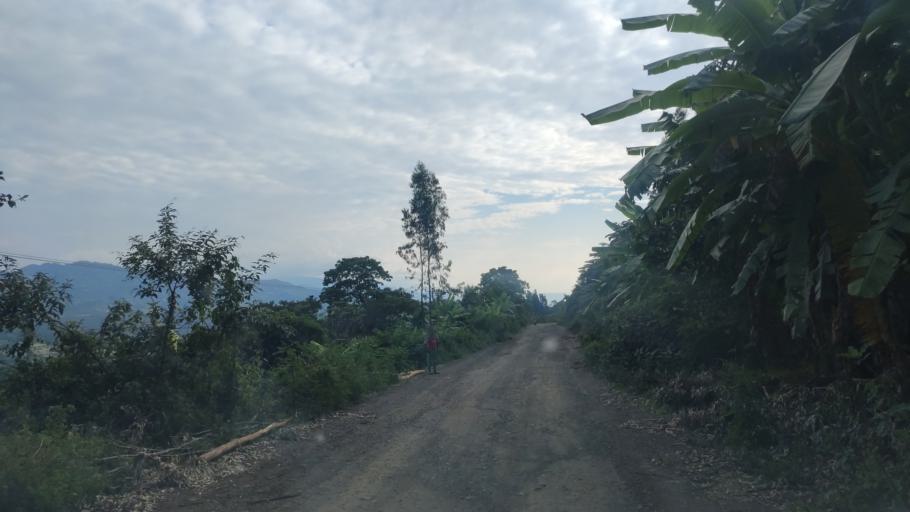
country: ET
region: Southern Nations, Nationalities, and People's Region
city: Arba Minch'
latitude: 6.4446
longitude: 37.3945
